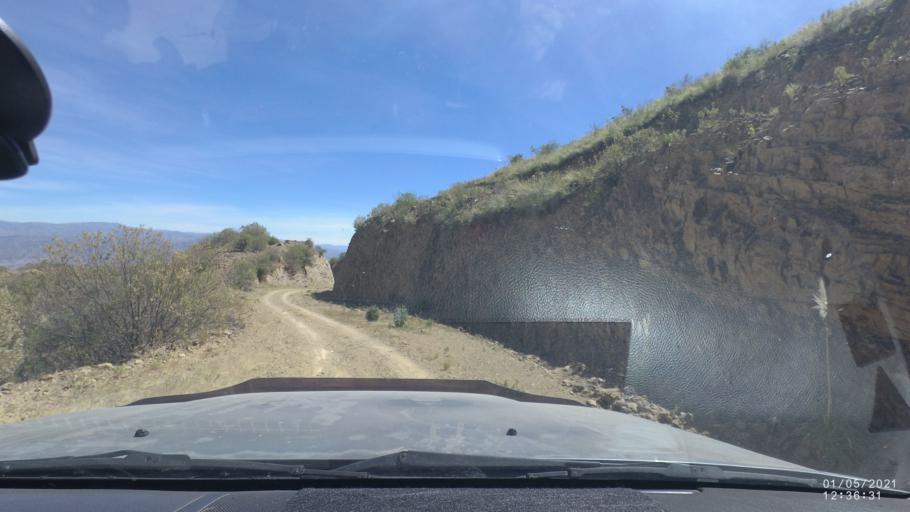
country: BO
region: Cochabamba
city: Capinota
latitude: -17.6776
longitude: -66.1565
